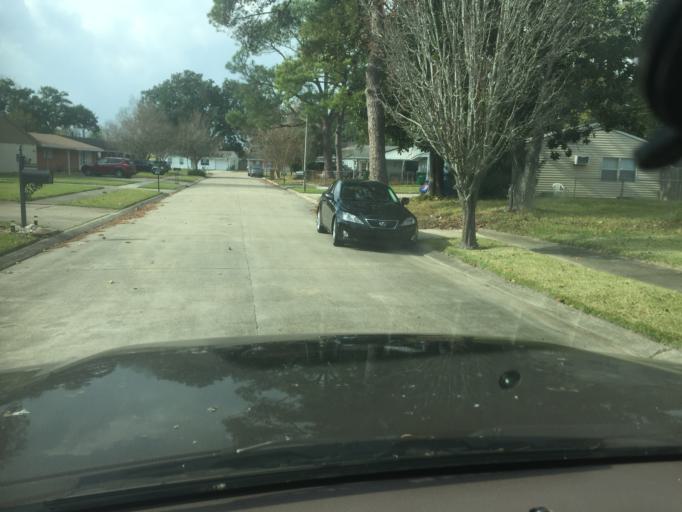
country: US
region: Louisiana
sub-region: Jefferson Parish
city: Avondale
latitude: 29.9140
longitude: -90.2044
